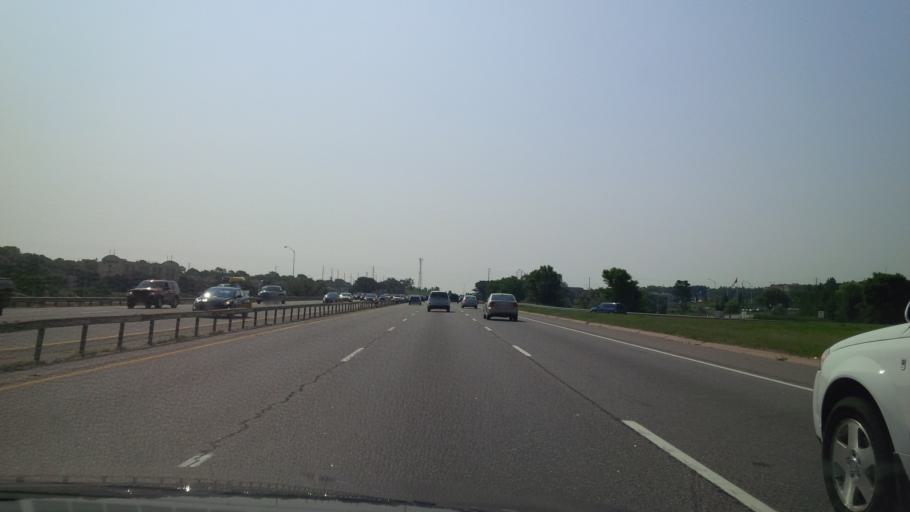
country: CA
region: Ontario
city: Barrie
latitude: 44.3636
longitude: -79.6992
